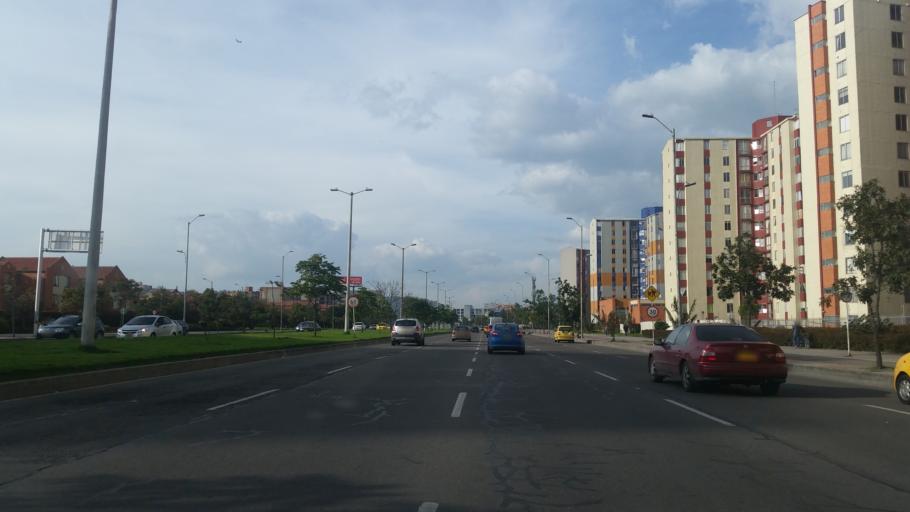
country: CO
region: Cundinamarca
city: Cota
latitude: 4.7443
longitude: -74.0650
